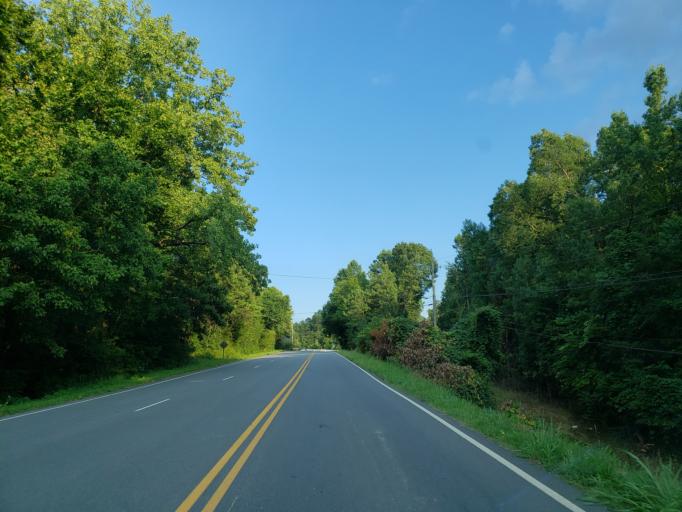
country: US
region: Georgia
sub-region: Polk County
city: Rockmart
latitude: 33.9801
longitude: -85.0351
